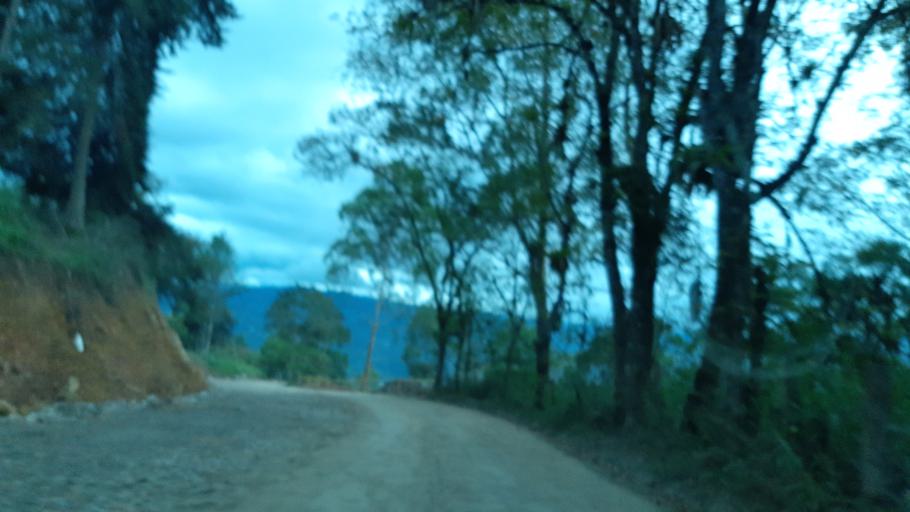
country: CO
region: Boyaca
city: Garagoa
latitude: 5.0856
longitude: -73.3580
